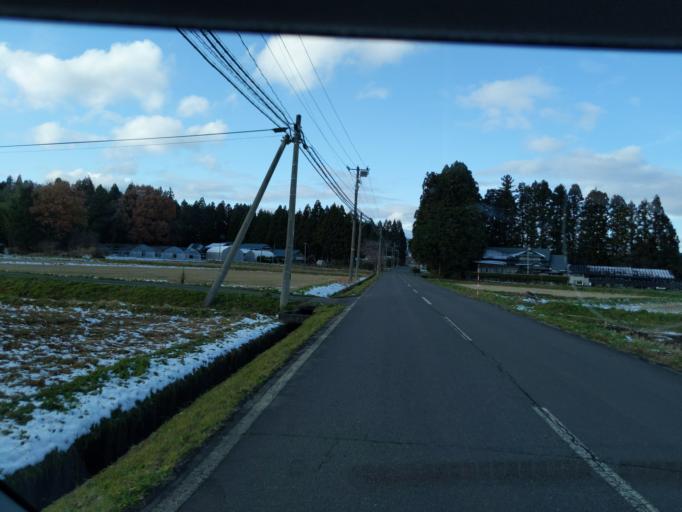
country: JP
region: Iwate
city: Kitakami
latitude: 39.2189
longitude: 141.0462
